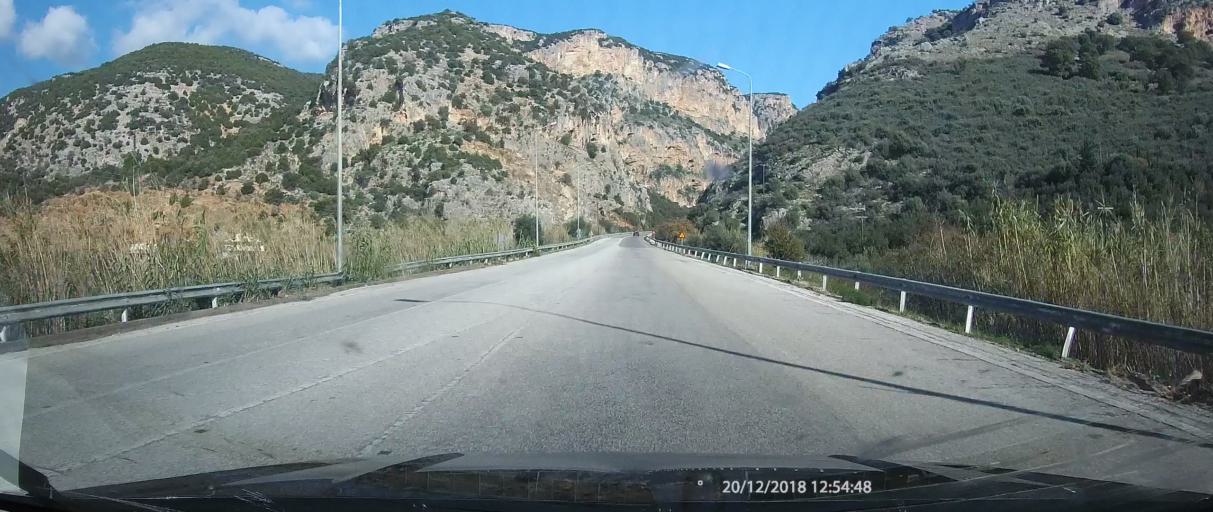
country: GR
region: West Greece
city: Aitoliko
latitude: 38.4949
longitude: 21.3612
